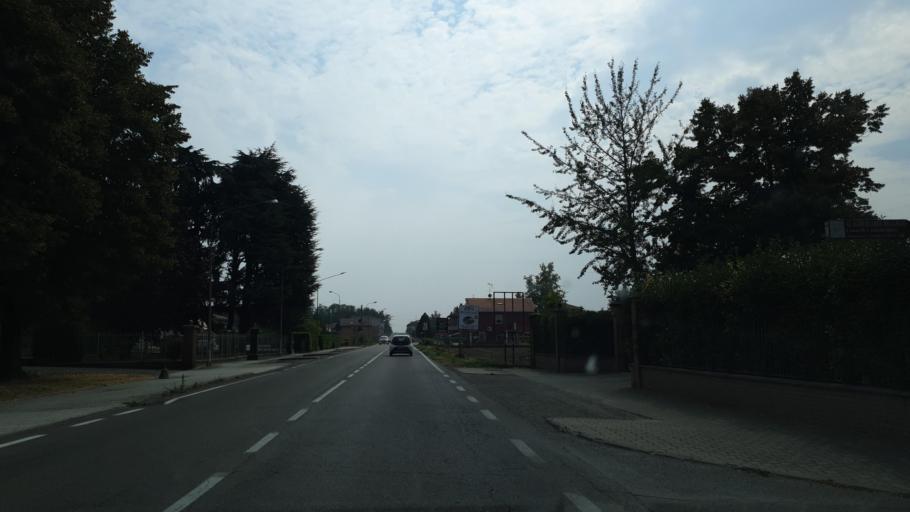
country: IT
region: Emilia-Romagna
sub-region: Provincia di Parma
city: Roccabianca
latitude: 44.9696
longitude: 10.2134
